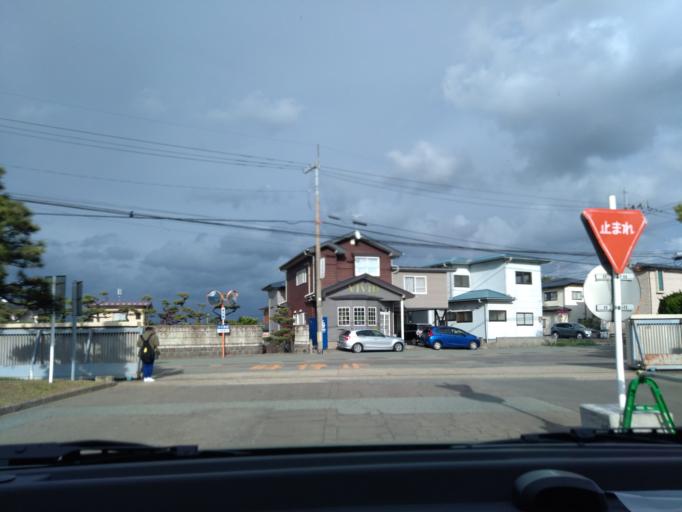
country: JP
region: Akita
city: Akita Shi
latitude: 39.7716
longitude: 140.0814
